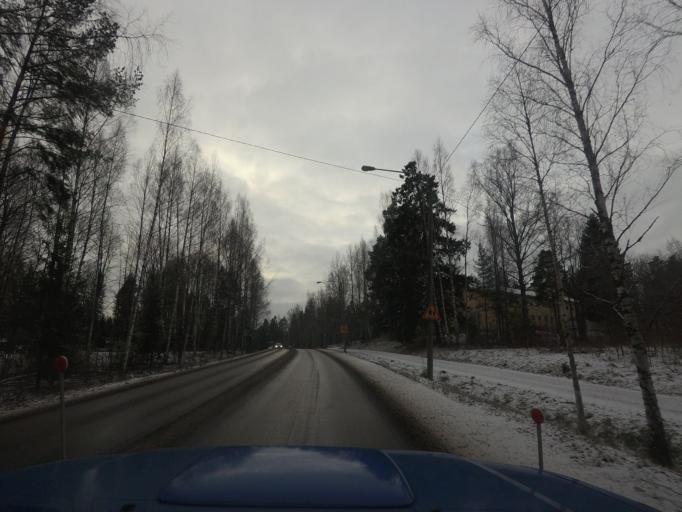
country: FI
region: Uusimaa
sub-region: Helsinki
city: Kilo
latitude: 60.2344
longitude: 24.7721
